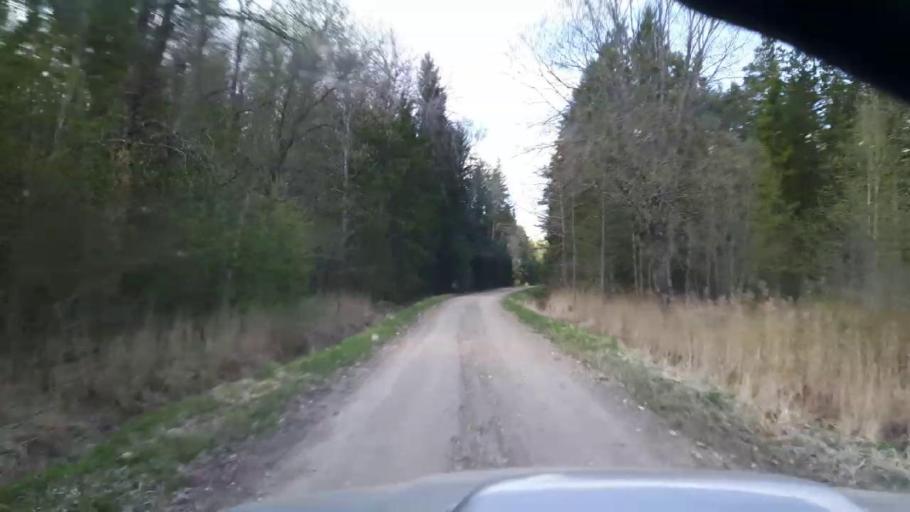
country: EE
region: Paernumaa
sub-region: Tootsi vald
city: Tootsi
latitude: 58.4433
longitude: 24.9355
